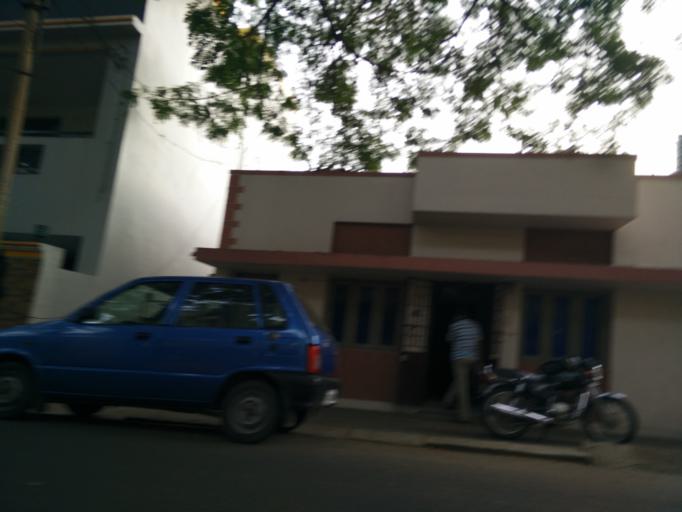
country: IN
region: Tamil Nadu
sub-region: Coimbatore
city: Coimbatore
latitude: 11.0269
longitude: 76.9418
